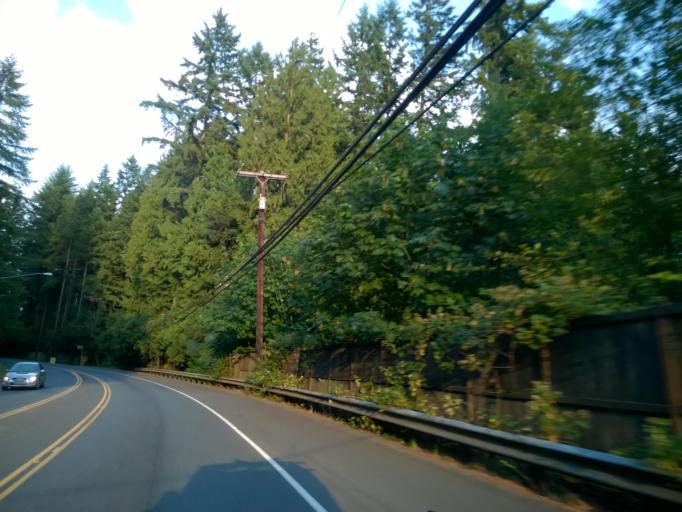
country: US
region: Washington
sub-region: King County
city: Cottage Lake
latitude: 47.7530
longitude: -122.0719
